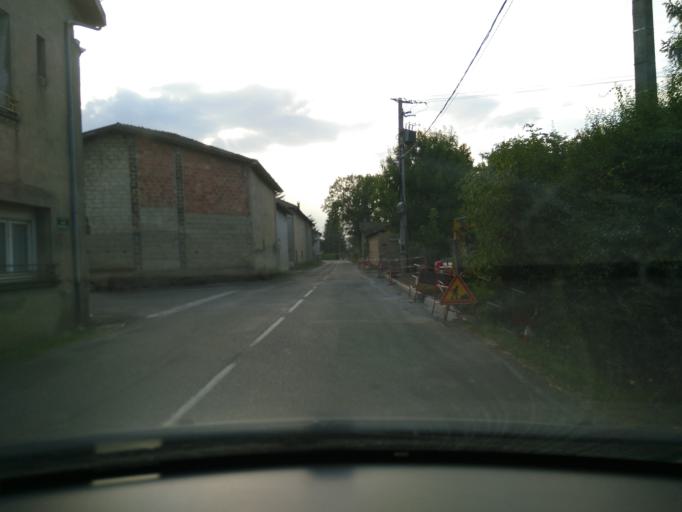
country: FR
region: Rhone-Alpes
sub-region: Departement de l'Isere
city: Viriville
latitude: 45.3945
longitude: 5.1628
